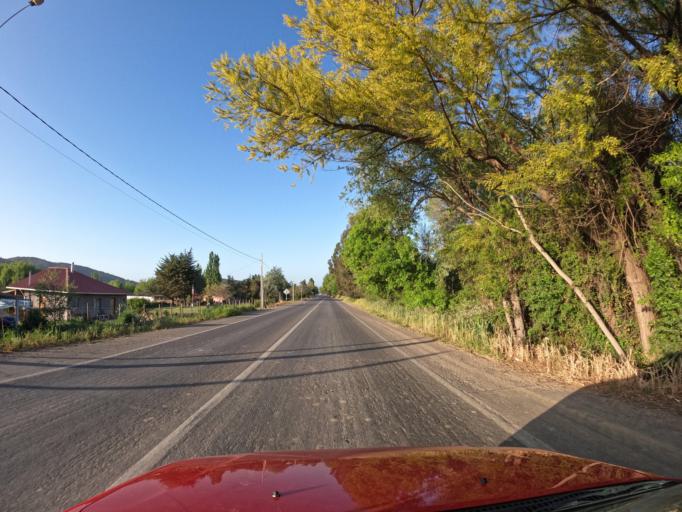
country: CL
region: O'Higgins
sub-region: Provincia de Colchagua
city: Santa Cruz
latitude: -34.3338
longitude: -71.3975
